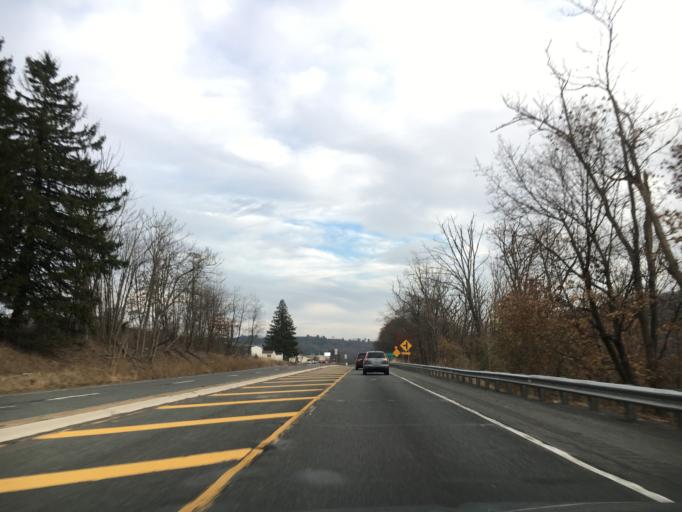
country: US
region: Pennsylvania
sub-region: Carbon County
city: Weissport East
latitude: 40.8230
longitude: -75.6907
